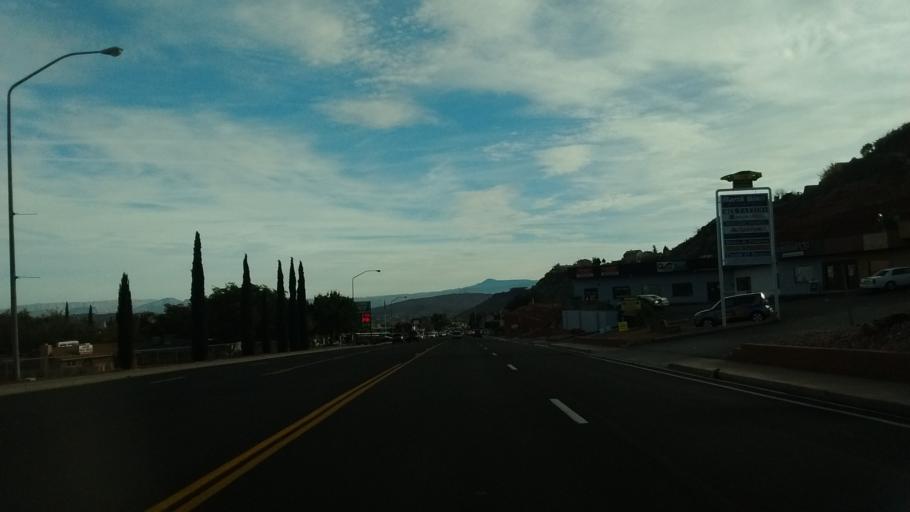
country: US
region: Utah
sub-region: Washington County
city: Saint George
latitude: 37.1162
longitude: -113.5967
